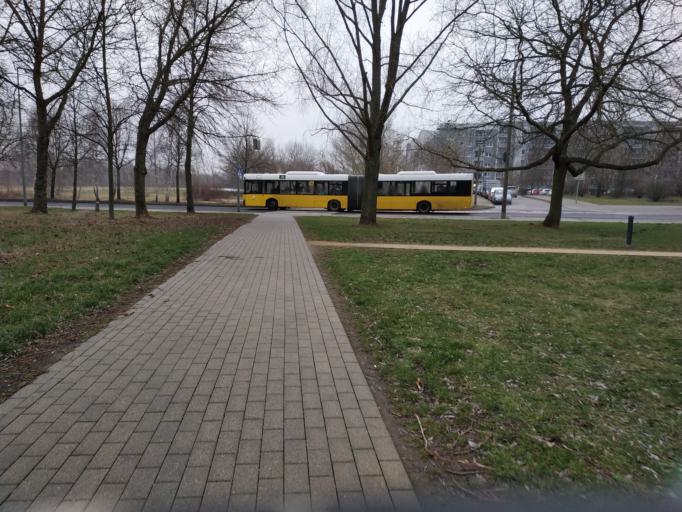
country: DE
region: Berlin
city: Marzahn
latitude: 52.5392
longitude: 13.5843
